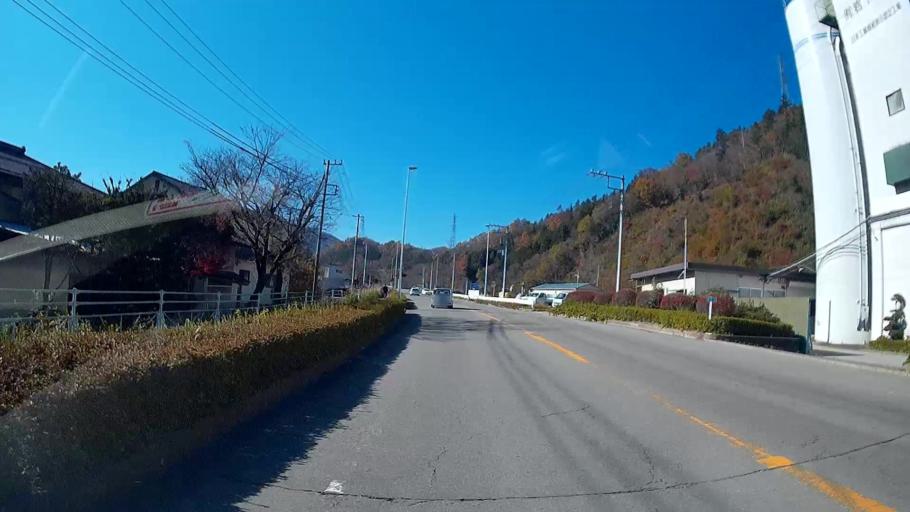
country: JP
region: Yamanashi
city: Otsuki
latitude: 35.5476
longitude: 138.9145
